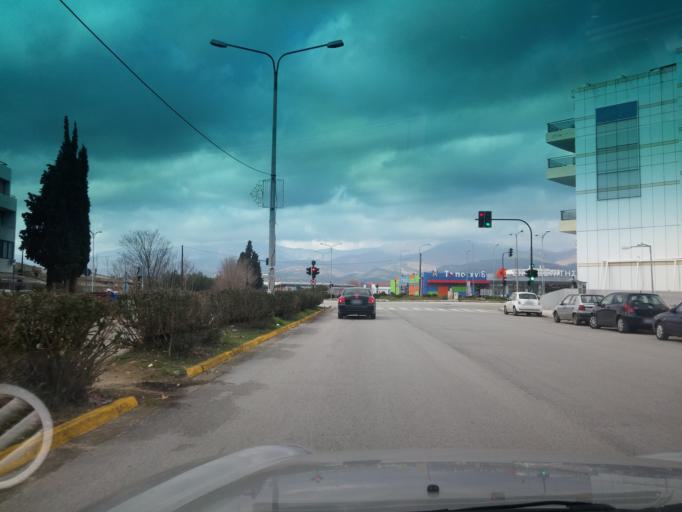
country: GR
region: East Macedonia and Thrace
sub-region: Nomos Rodopis
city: Komotini
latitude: 41.1251
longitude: 25.3935
